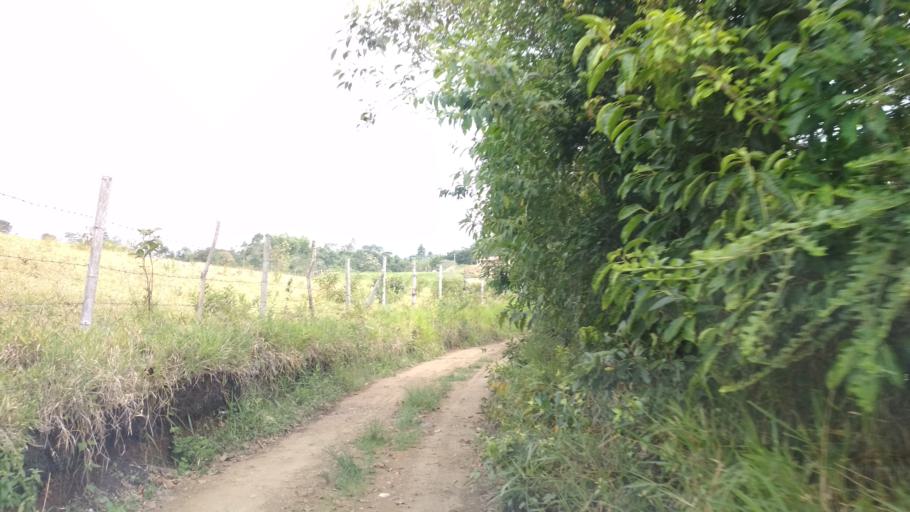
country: CO
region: Cauca
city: Lopez
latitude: 2.4055
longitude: -76.7138
